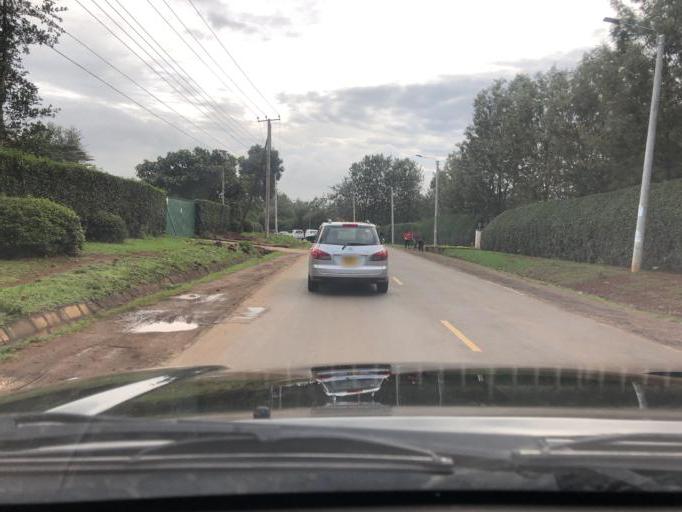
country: KE
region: Kajiado
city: Ngong
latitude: -1.3395
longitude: 36.7148
